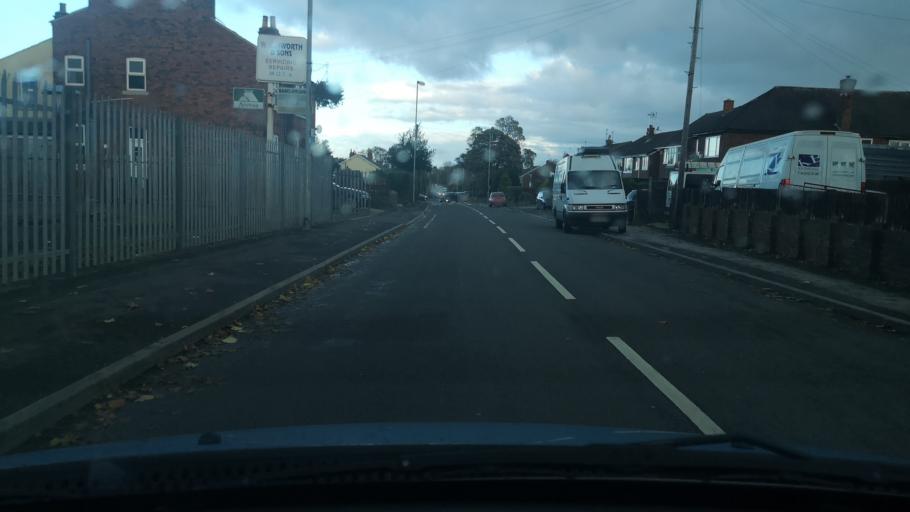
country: GB
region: England
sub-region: City and Borough of Wakefield
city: Crigglestone
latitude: 53.6325
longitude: -1.5205
